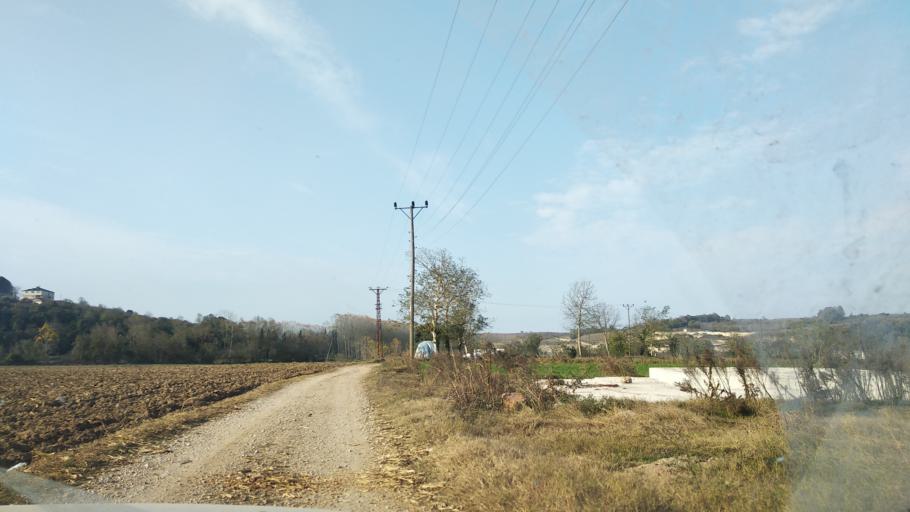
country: TR
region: Sakarya
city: Karasu
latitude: 41.0900
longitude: 30.5957
